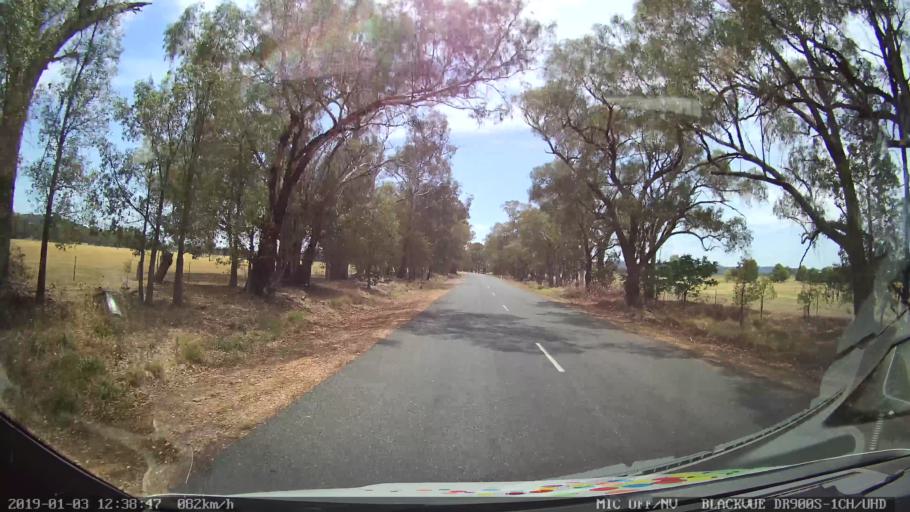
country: AU
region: New South Wales
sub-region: Weddin
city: Grenfell
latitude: -33.8307
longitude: 148.1998
